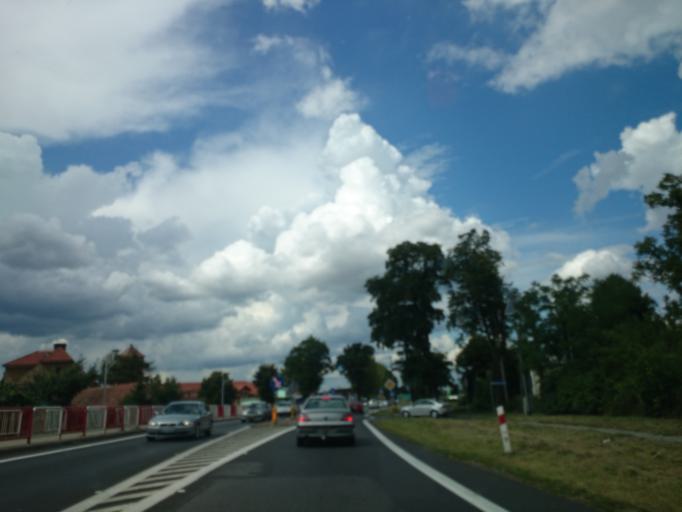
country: PL
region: Lubusz
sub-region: Powiat nowosolski
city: Nowe Miasteczko
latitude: 51.6898
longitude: 15.7362
